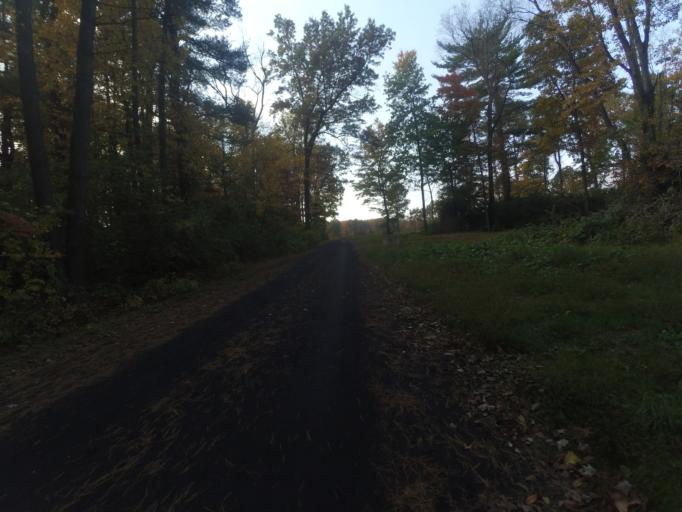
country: US
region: Pennsylvania
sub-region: Centre County
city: Park Forest Village
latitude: 40.8312
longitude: -77.8875
